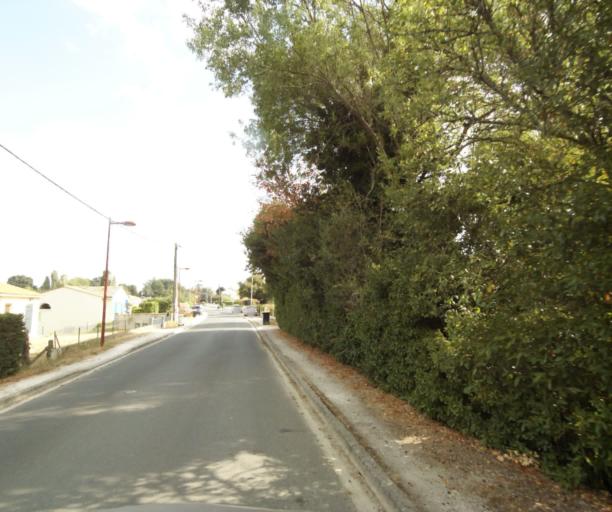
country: FR
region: Aquitaine
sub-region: Departement de la Gironde
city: Creon
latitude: 44.7668
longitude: -0.3516
